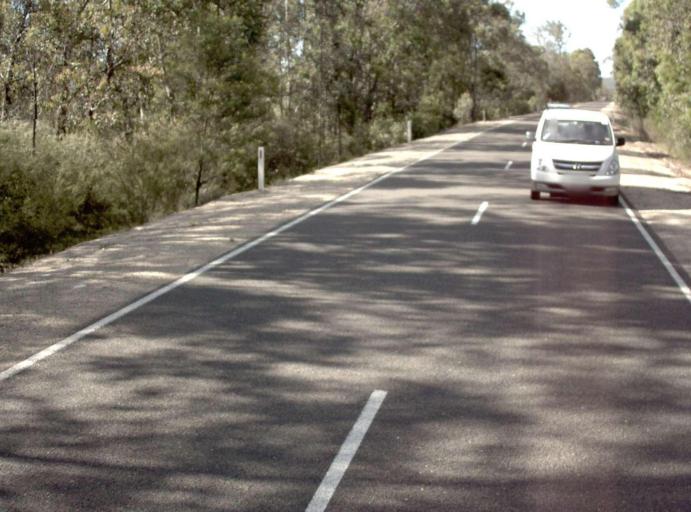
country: AU
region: Victoria
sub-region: East Gippsland
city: Lakes Entrance
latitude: -37.5865
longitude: 148.1235
